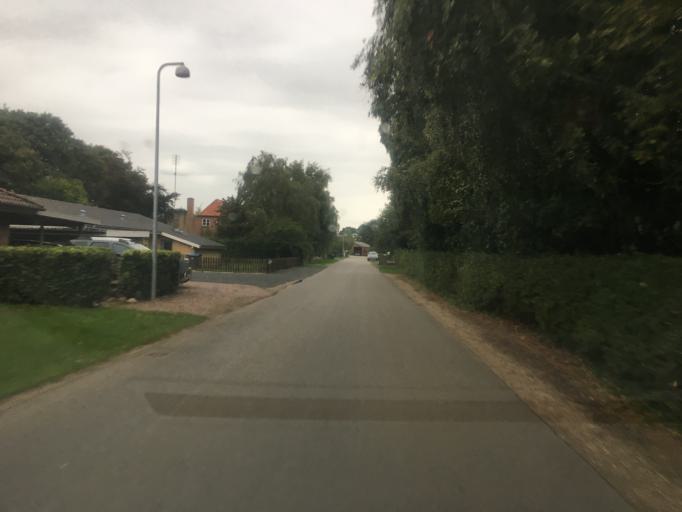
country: DE
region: Schleswig-Holstein
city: Ellhoft
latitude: 54.9481
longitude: 8.9689
